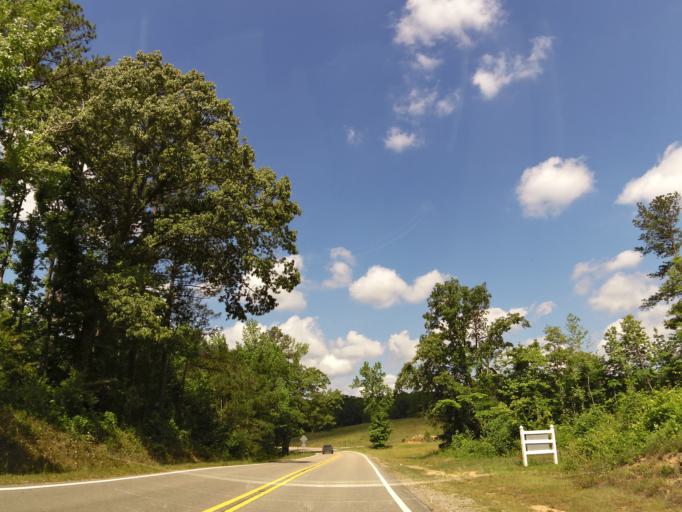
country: US
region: Alabama
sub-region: Marion County
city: Guin
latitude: 33.9960
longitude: -87.8645
